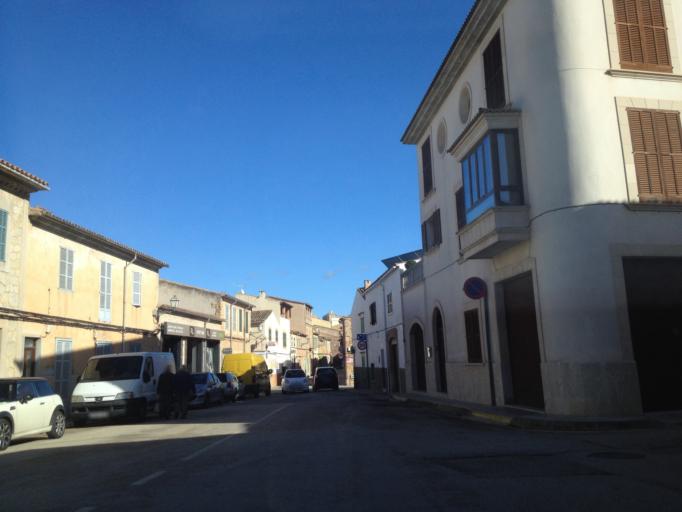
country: ES
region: Balearic Islands
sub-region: Illes Balears
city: Arta
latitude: 39.6934
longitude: 3.3473
